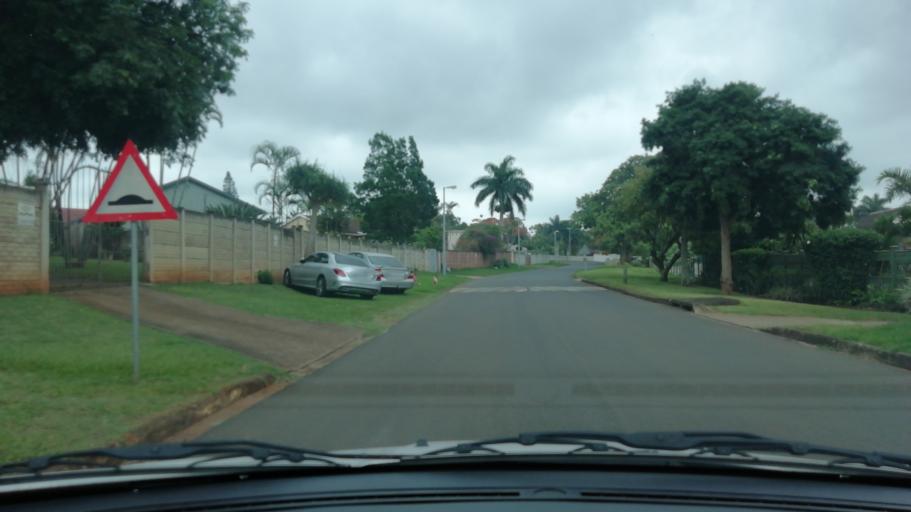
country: ZA
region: KwaZulu-Natal
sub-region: uThungulu District Municipality
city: Empangeni
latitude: -28.7641
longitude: 31.8968
